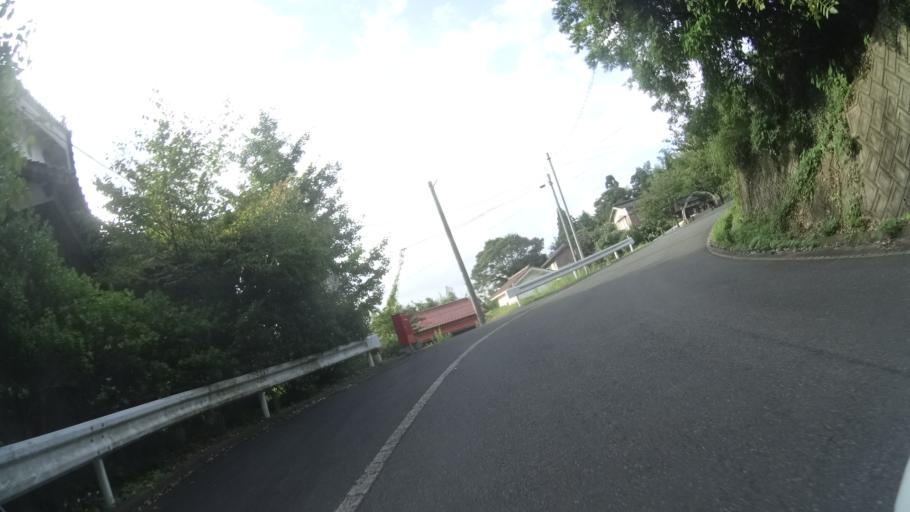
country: JP
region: Tottori
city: Kurayoshi
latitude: 35.4864
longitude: 133.9016
